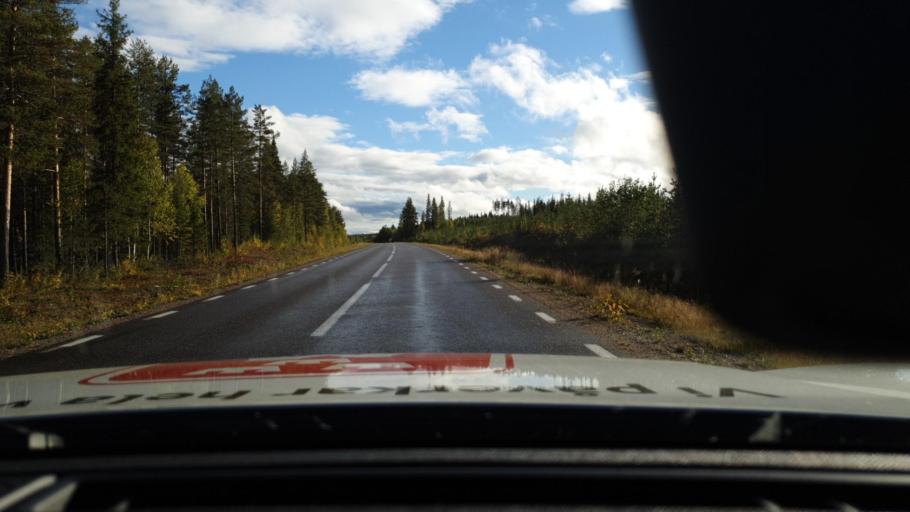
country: SE
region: Norrbotten
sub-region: Overkalix Kommun
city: OEverkalix
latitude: 66.7545
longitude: 22.6734
